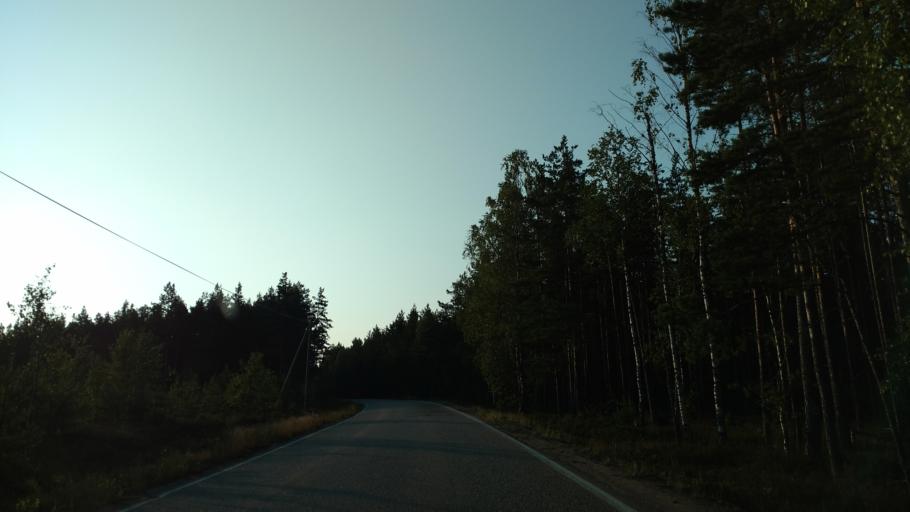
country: FI
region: Varsinais-Suomi
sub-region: Salo
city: Saerkisalo
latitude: 60.1967
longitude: 22.9425
